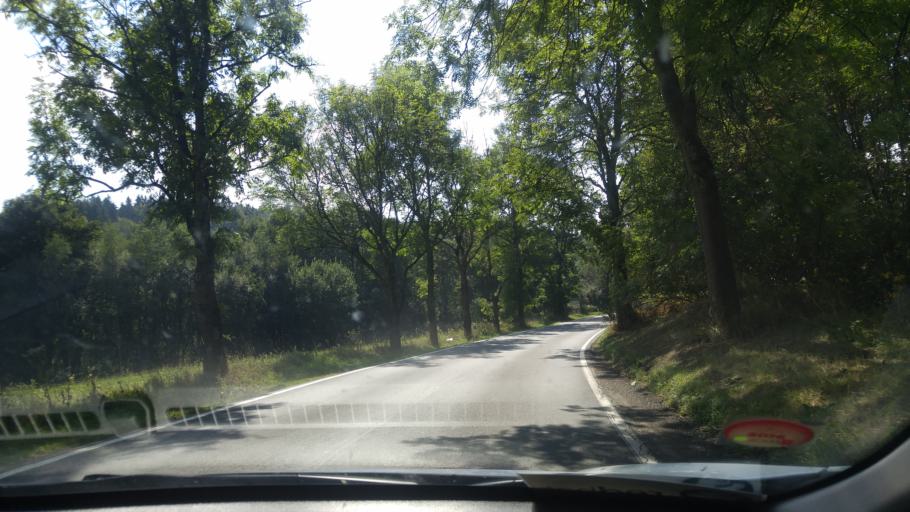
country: CZ
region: Olomoucky
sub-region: Okres Sumperk
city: Stare Mesto
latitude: 50.1742
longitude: 17.0390
